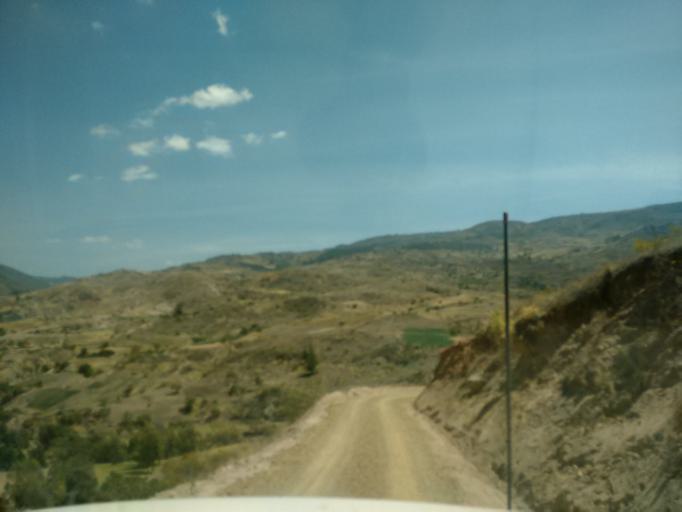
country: CO
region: Boyaca
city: Sachica
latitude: 5.5837
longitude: -73.5145
